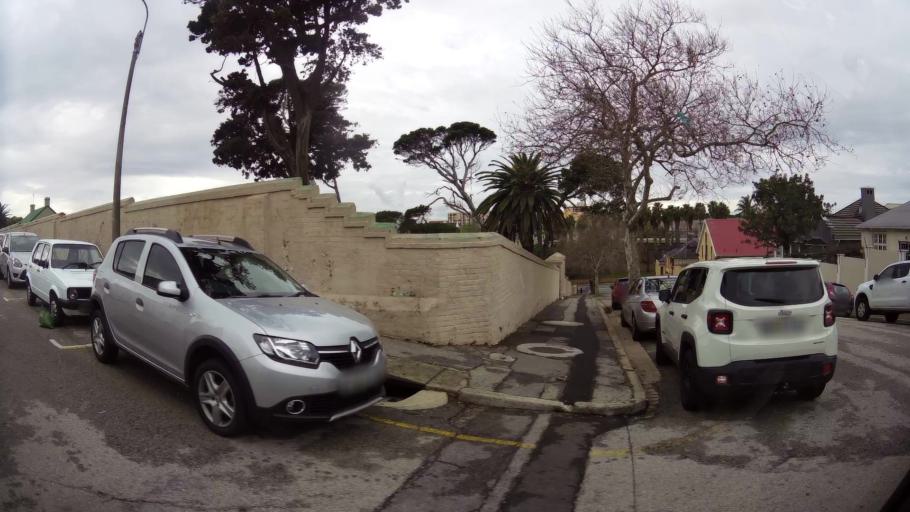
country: ZA
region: Eastern Cape
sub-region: Nelson Mandela Bay Metropolitan Municipality
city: Port Elizabeth
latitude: -33.9602
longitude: 25.6143
